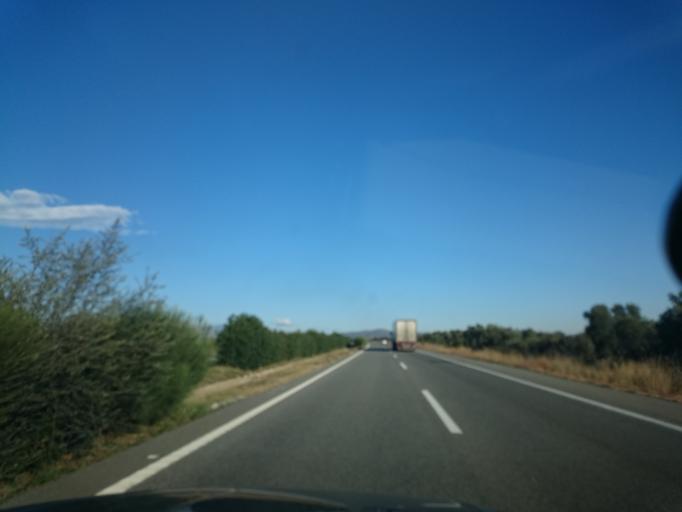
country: ES
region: Catalonia
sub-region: Provincia de Tarragona
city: Alcanar
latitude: 40.5300
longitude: 0.4184
